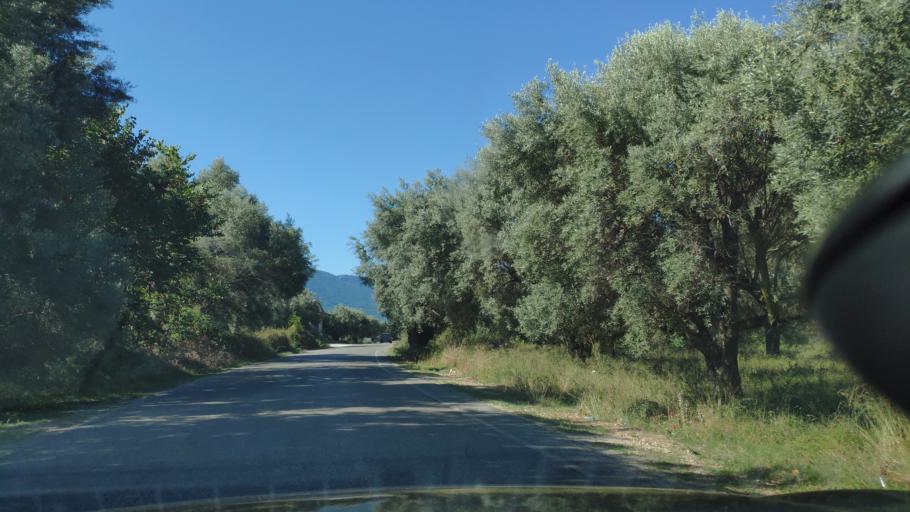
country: GR
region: West Greece
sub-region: Nomos Aitolias kai Akarnanias
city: Kandila
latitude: 38.6977
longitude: 20.9479
